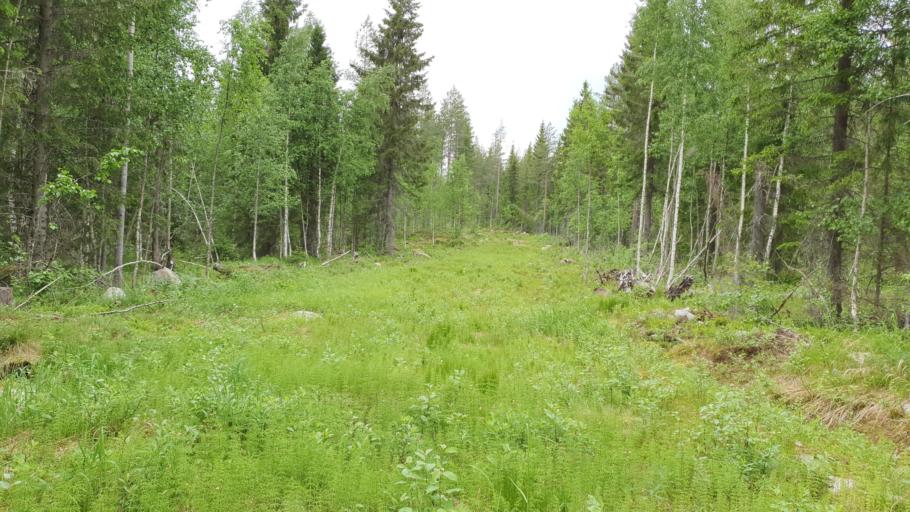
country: FI
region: Kainuu
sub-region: Kehys-Kainuu
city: Kuhmo
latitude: 64.4428
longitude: 29.6876
